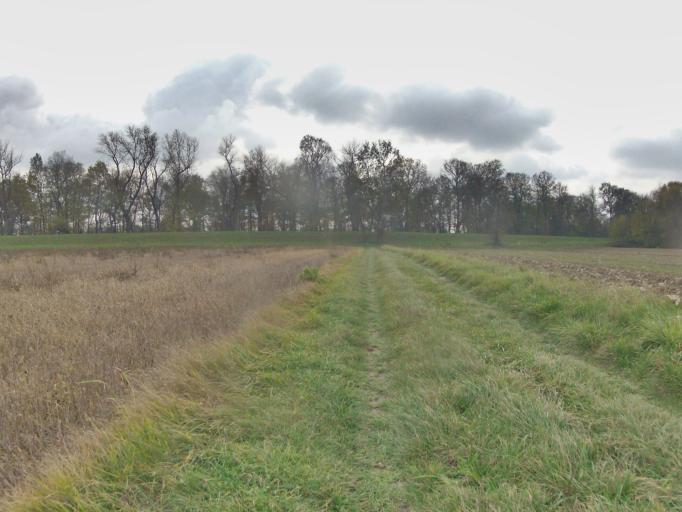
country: PL
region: Lesser Poland Voivodeship
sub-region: Powiat wielicki
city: Wegrzce Wielkie
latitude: 50.0465
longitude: 20.1086
